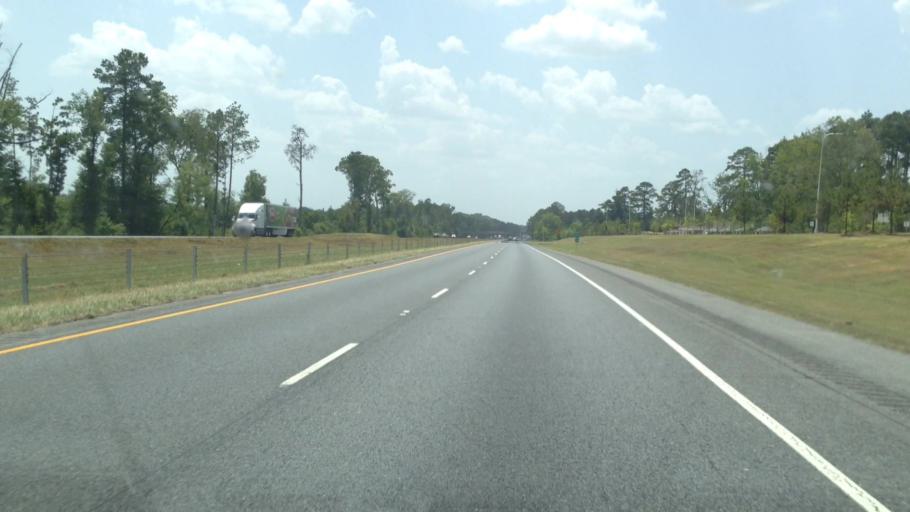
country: US
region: Louisiana
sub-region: Lincoln Parish
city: Ruston
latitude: 32.5287
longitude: -92.4448
